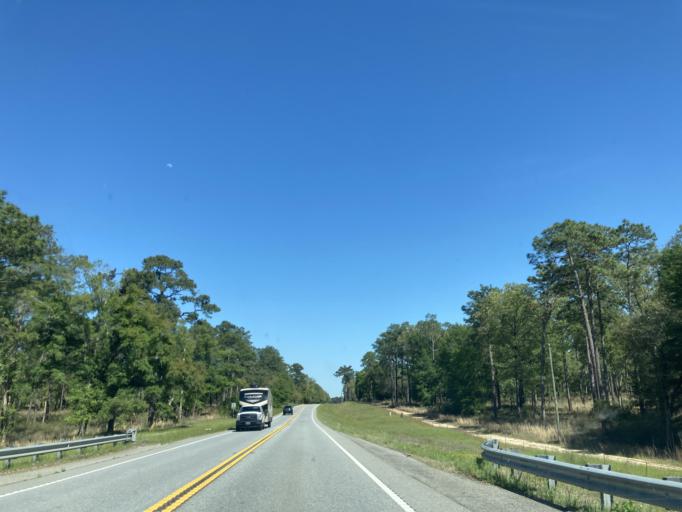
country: US
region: Georgia
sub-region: Baker County
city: Newton
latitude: 31.2135
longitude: -84.4721
